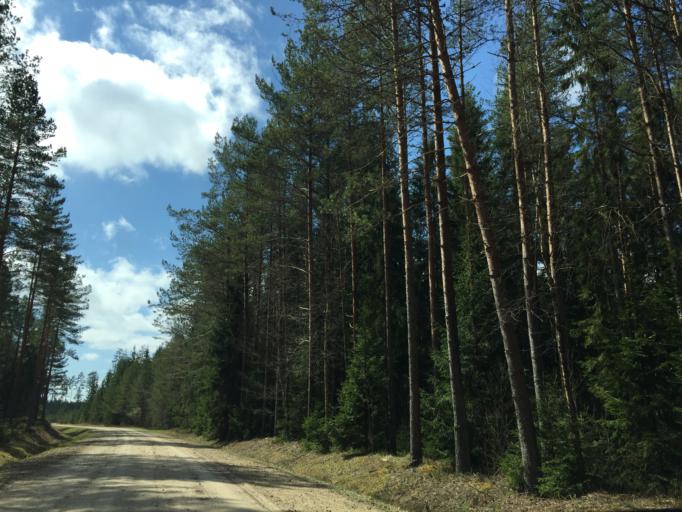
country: EE
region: Valgamaa
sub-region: Valga linn
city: Valga
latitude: 57.6092
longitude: 26.1569
